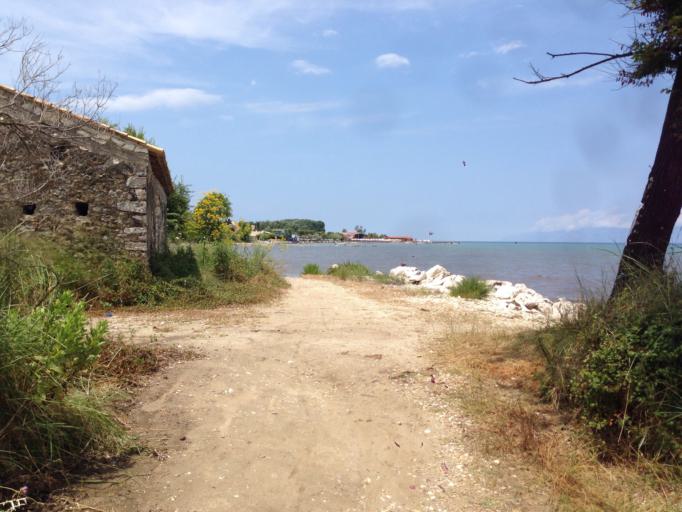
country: GR
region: Ionian Islands
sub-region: Nomos Kerkyras
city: Acharavi
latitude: 39.7934
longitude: 19.7847
